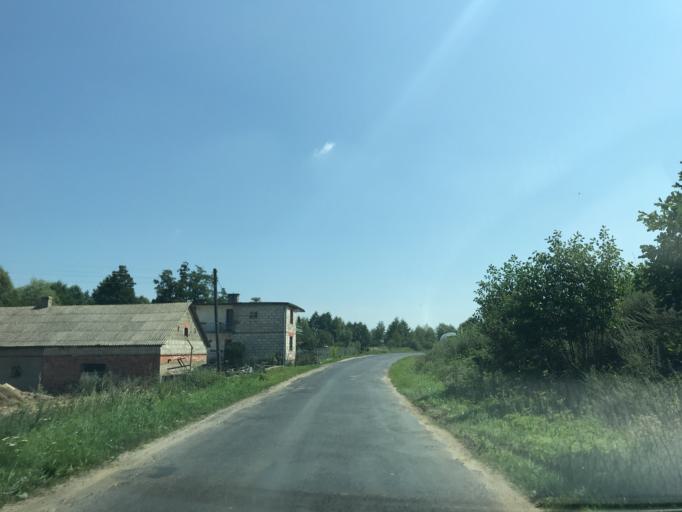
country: PL
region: Kujawsko-Pomorskie
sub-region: Powiat golubsko-dobrzynski
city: Zbojno
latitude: 52.9975
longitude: 19.2090
